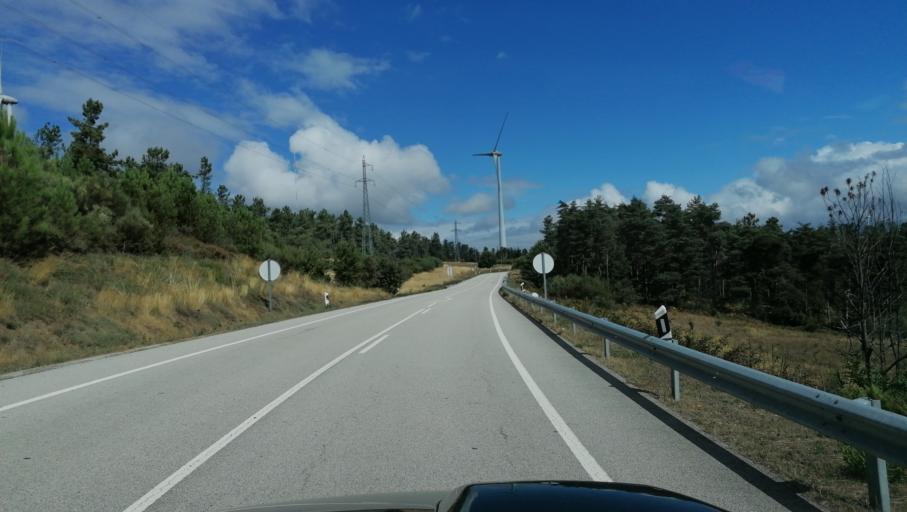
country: PT
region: Vila Real
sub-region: Vila Pouca de Aguiar
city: Vila Pouca de Aguiar
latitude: 41.5212
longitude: -7.5942
